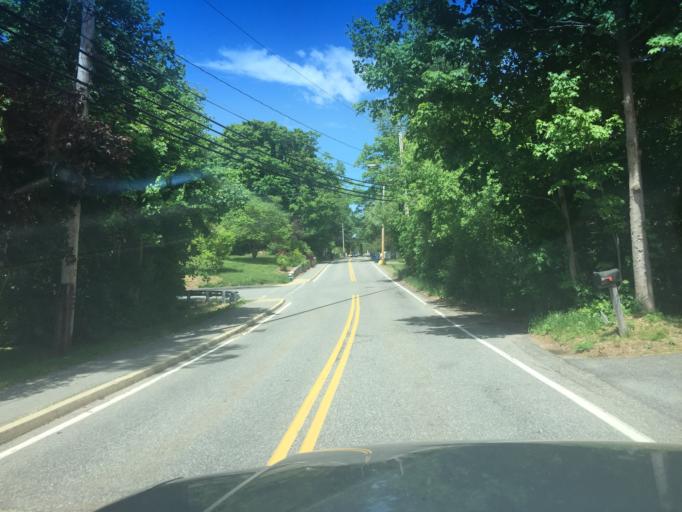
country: US
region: Massachusetts
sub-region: Norfolk County
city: Medway
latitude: 42.1432
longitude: -71.4215
